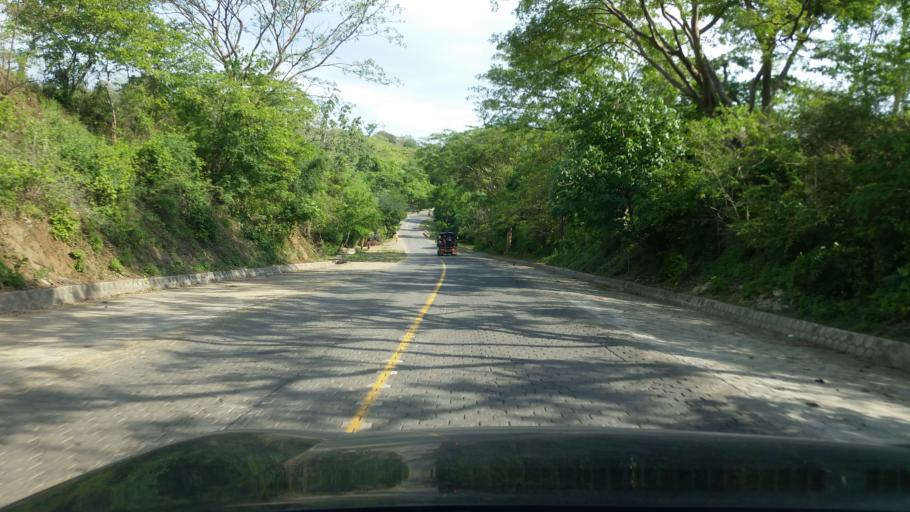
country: NI
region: Managua
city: Carlos Fonseca Amador
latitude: 11.9039
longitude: -86.5104
